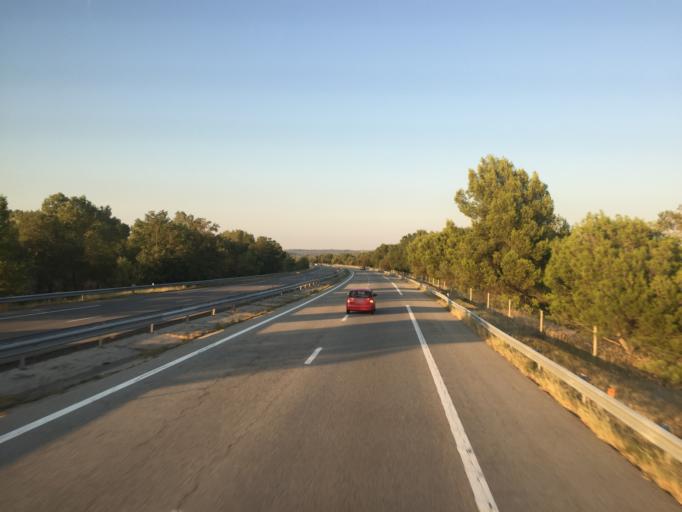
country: FR
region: Provence-Alpes-Cote d'Azur
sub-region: Departement des Alpes-de-Haute-Provence
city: Sainte-Tulle
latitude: 43.7708
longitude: 5.7925
